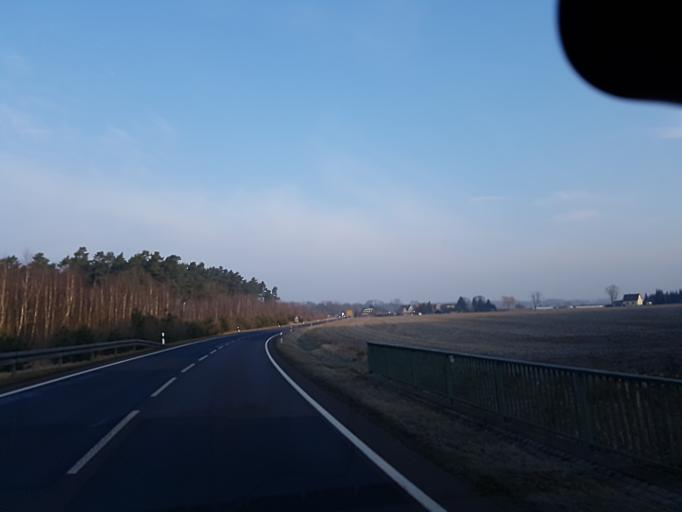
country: DE
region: Brandenburg
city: Wiesenburg
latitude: 52.0838
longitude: 12.4456
